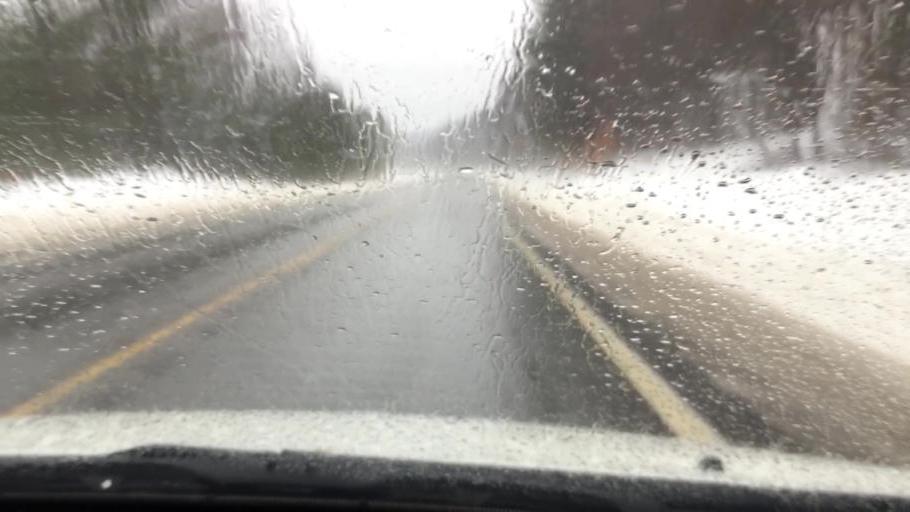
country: US
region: Michigan
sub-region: Antrim County
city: Mancelona
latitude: 45.0169
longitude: -85.0644
